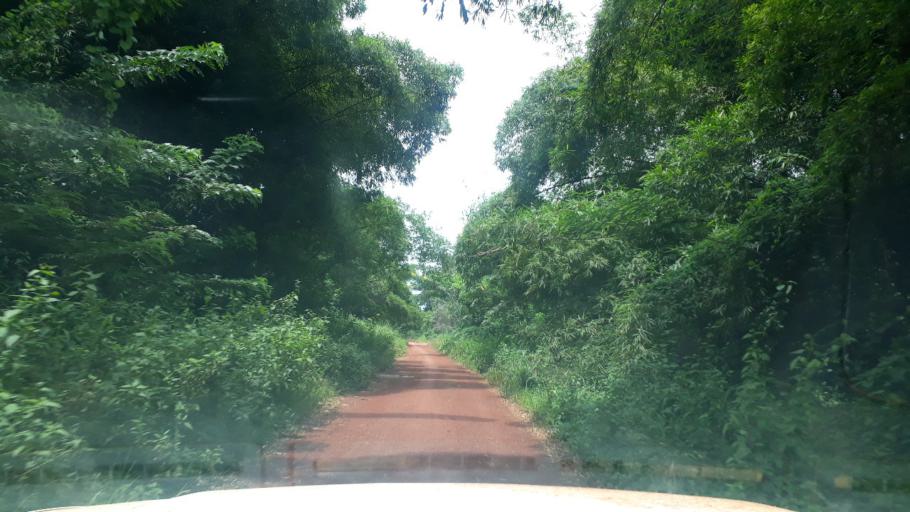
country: CD
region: Eastern Province
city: Aketi
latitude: 2.9341
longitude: 24.0946
